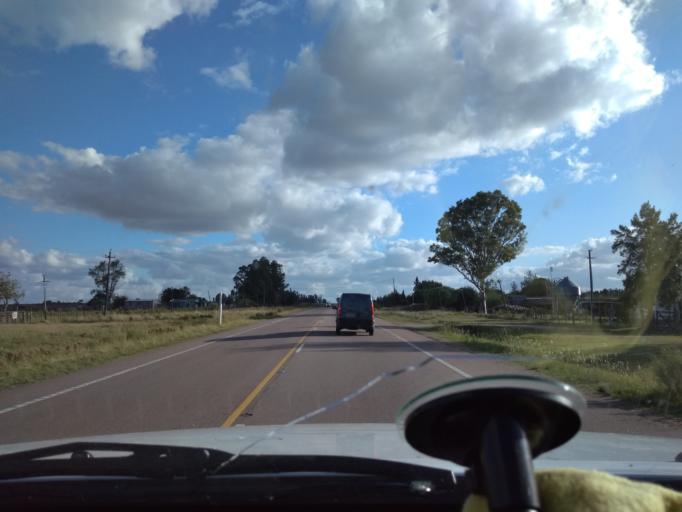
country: UY
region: Canelones
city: Tala
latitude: -34.4322
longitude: -55.8202
